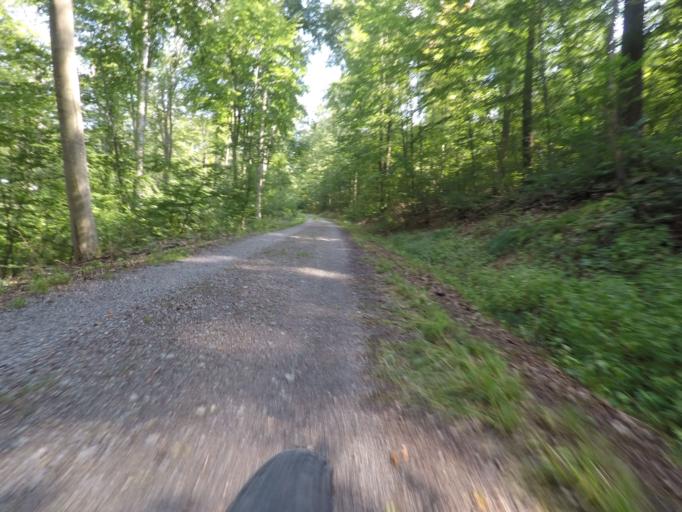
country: DE
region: Baden-Wuerttemberg
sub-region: Regierungsbezirk Stuttgart
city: Steinenbronn
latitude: 48.6784
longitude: 9.1053
